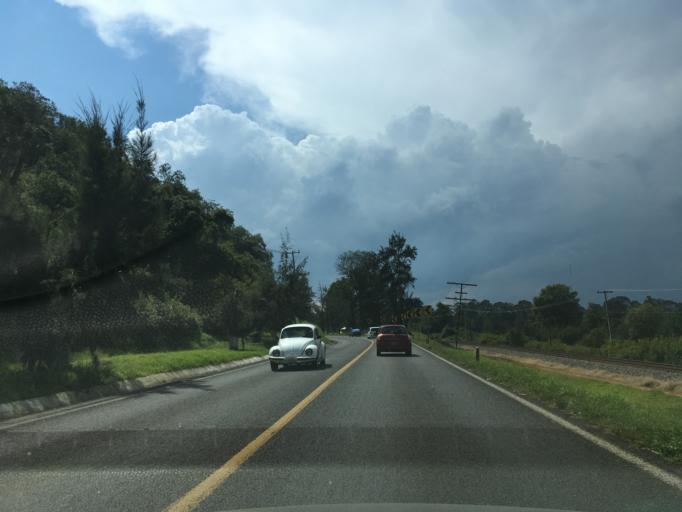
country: MX
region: Michoacan
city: Patzcuaro
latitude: 19.5443
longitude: -101.6055
